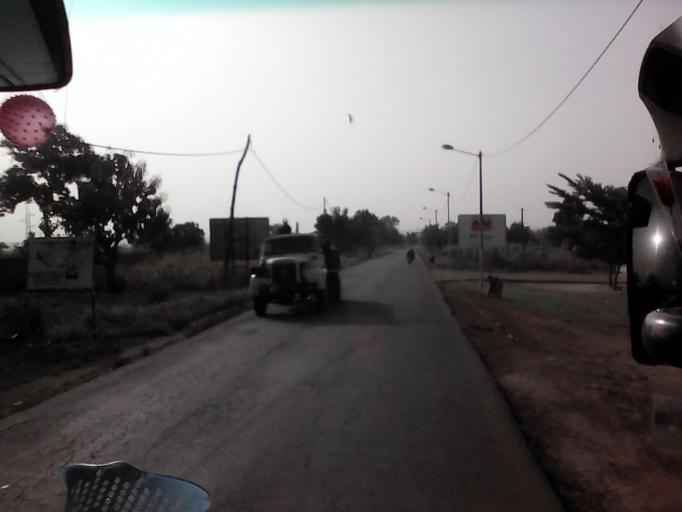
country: TG
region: Kara
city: Kara
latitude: 9.5266
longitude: 1.2055
